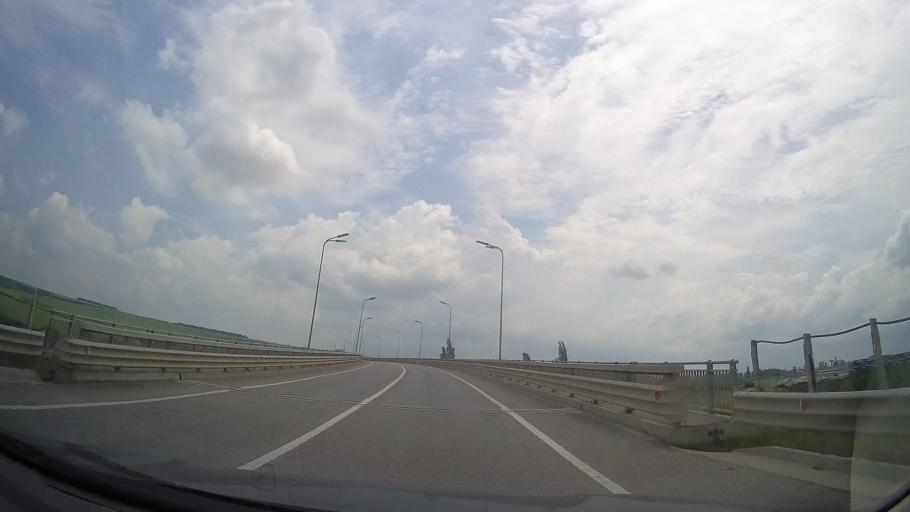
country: RO
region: Timis
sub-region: Comuna Costeiu
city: Costeiu
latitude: 45.7211
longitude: 21.8744
